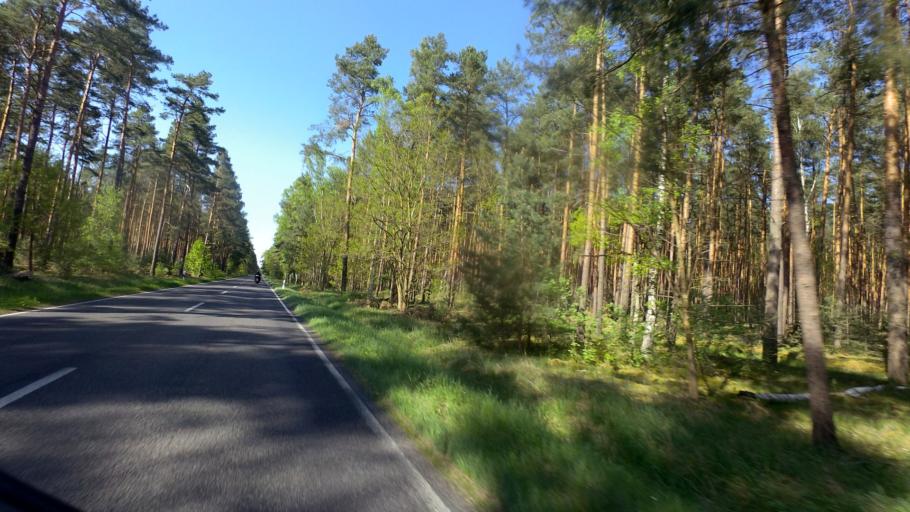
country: DE
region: Brandenburg
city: Gross Koris
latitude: 52.2025
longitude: 13.6929
